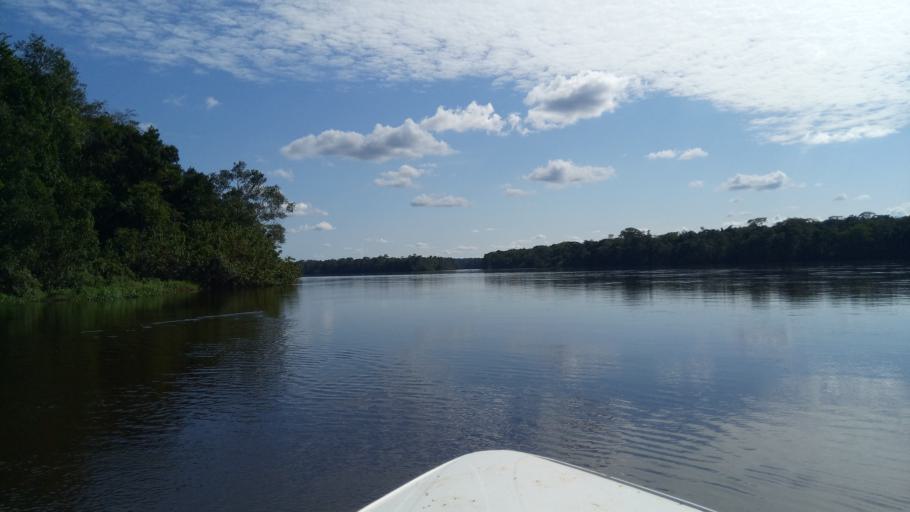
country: CD
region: Eastern Province
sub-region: Sous-Region de la Tshopo
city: Yangambi
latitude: 0.5320
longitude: 24.1967
